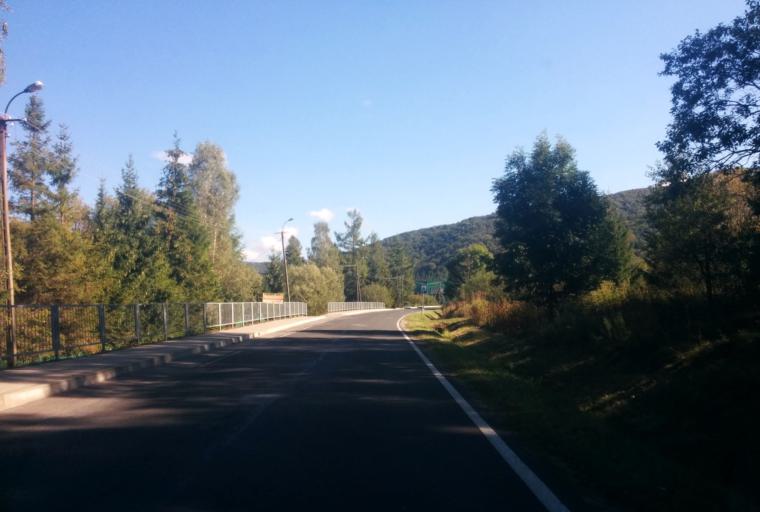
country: PL
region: Subcarpathian Voivodeship
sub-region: Powiat bieszczadzki
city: Lutowiska
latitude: 49.1077
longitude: 22.6514
